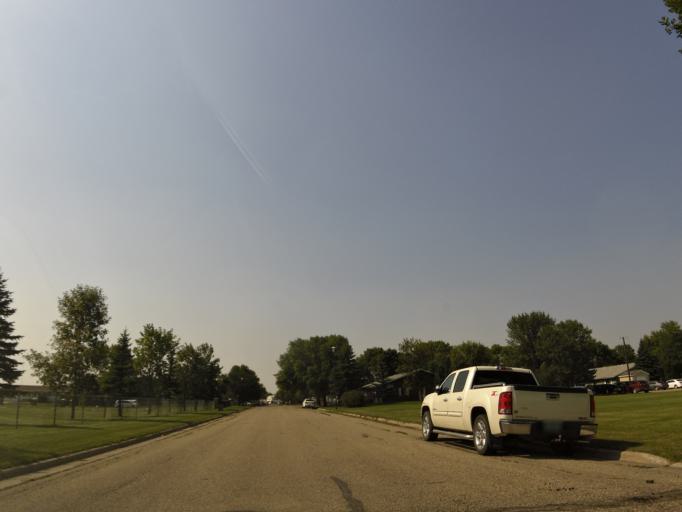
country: US
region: North Dakota
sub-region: Walsh County
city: Grafton
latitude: 48.4144
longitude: -97.4009
